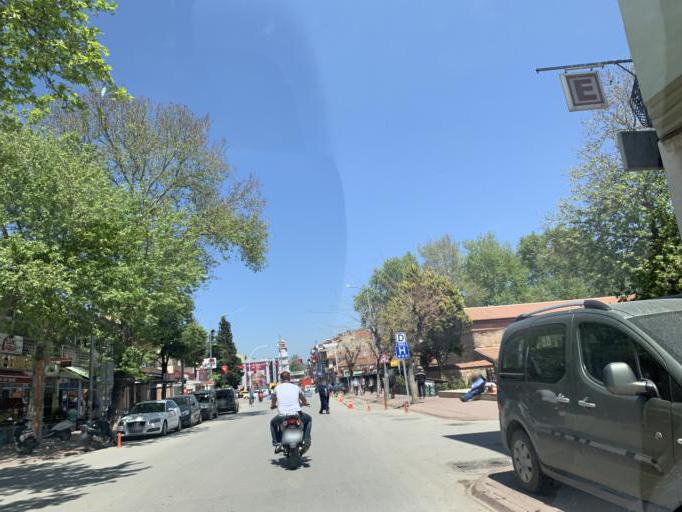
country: TR
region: Bursa
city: Iznik
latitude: 40.4287
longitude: 29.7198
